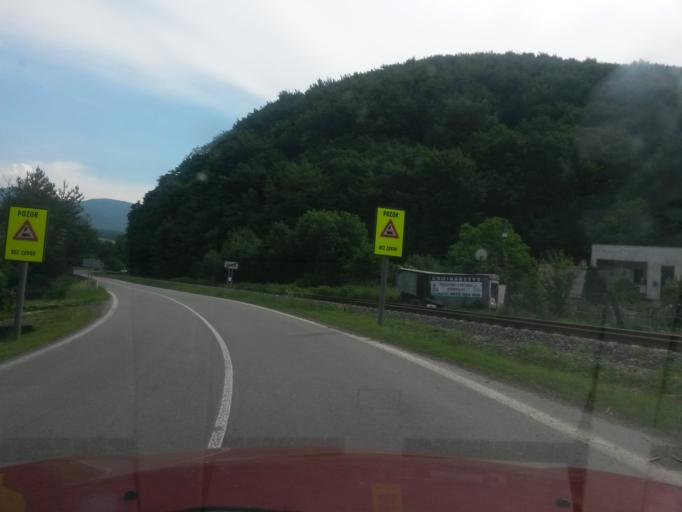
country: SK
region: Presovsky
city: Snina
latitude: 48.9928
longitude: 22.2142
